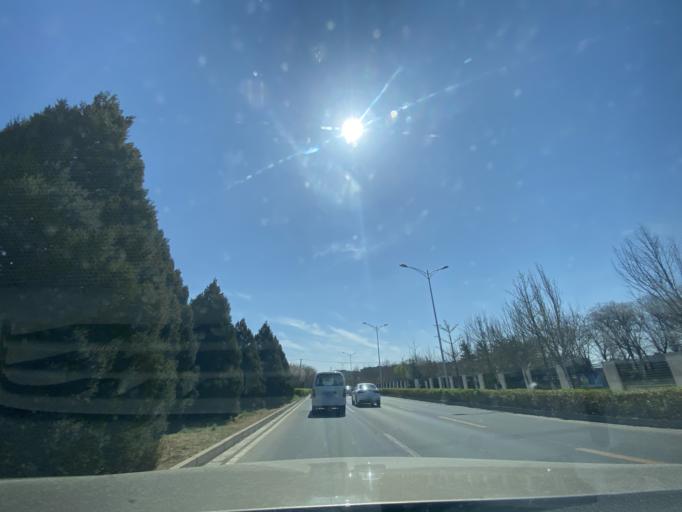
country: CN
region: Beijing
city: Sijiqing
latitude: 39.9363
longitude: 116.2425
